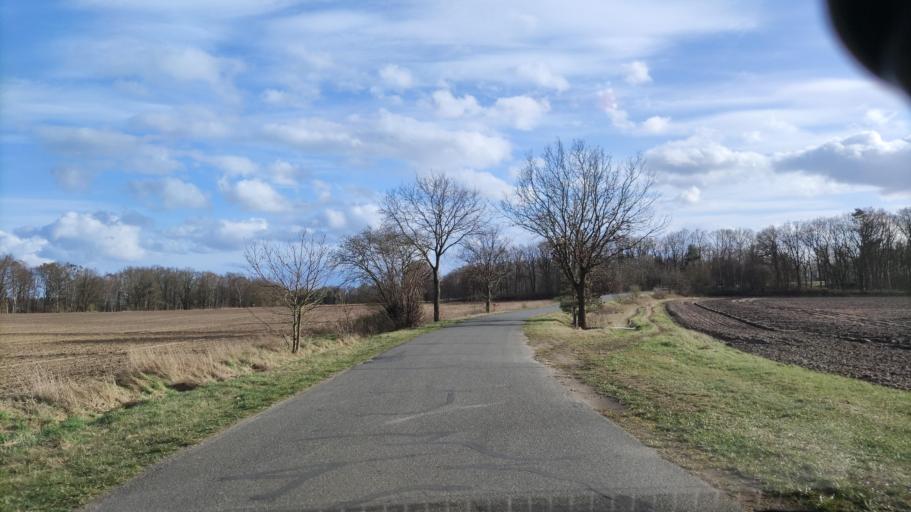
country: DE
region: Lower Saxony
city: Jelmstorf
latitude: 53.1270
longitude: 10.5207
